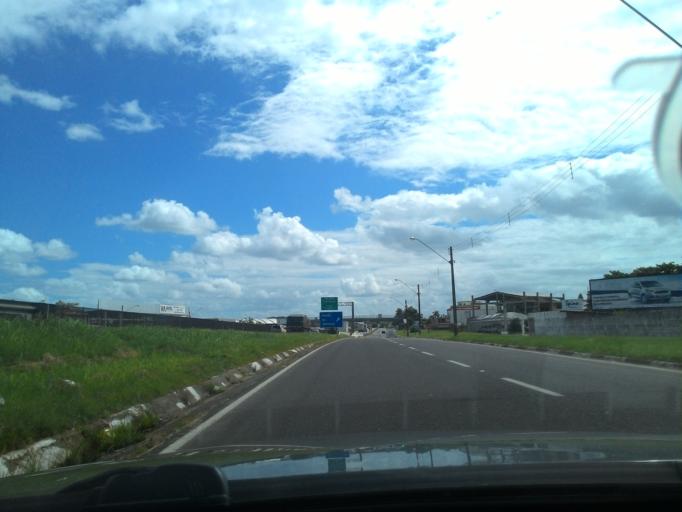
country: BR
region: Sao Paulo
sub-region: Registro
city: Registro
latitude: -24.4982
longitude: -47.8428
